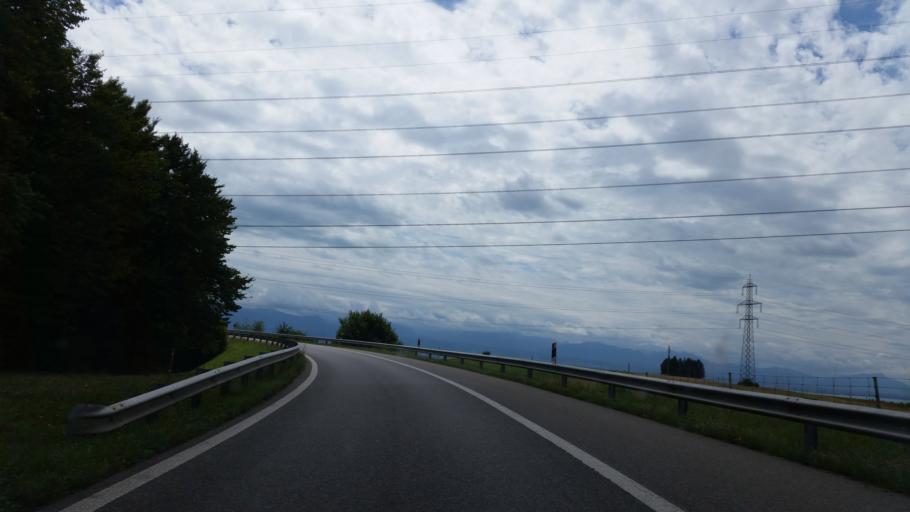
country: CH
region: Vaud
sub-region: Ouest Lausannois District
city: Bussigny
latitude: 46.5641
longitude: 6.5579
